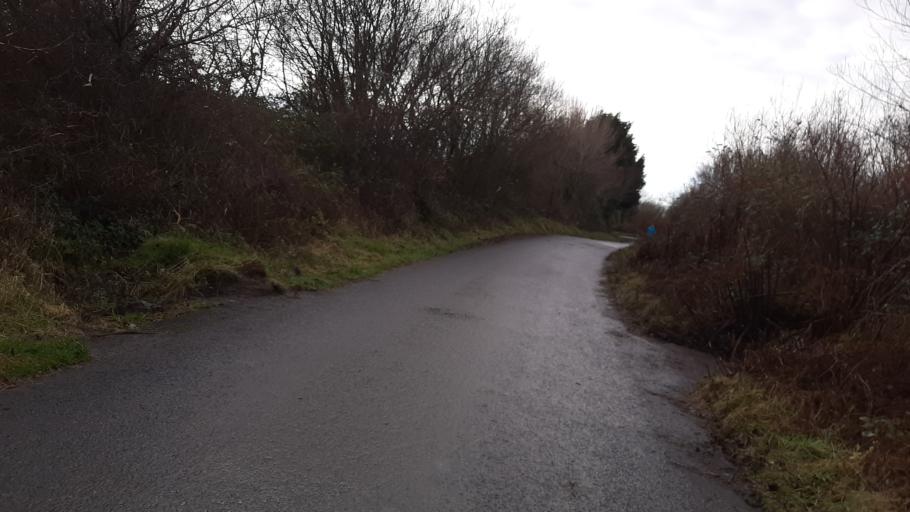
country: IE
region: Connaught
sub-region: County Galway
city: Gaillimh
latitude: 53.3186
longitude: -9.0641
